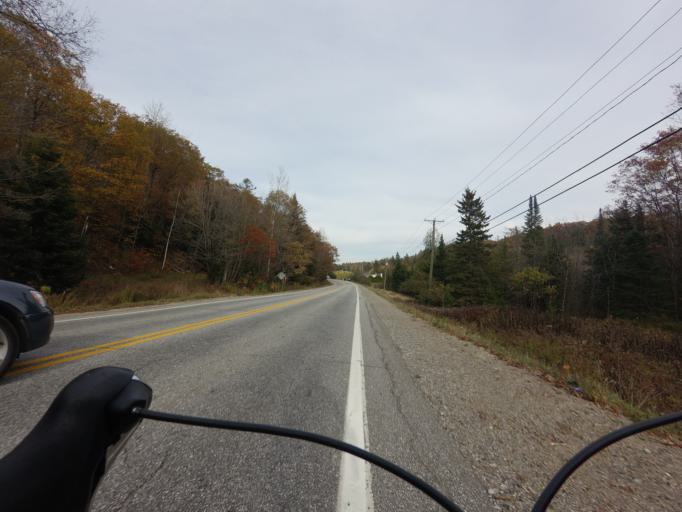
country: CA
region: Quebec
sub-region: Outaouais
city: Val-des-Monts
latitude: 45.6761
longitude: -75.7280
